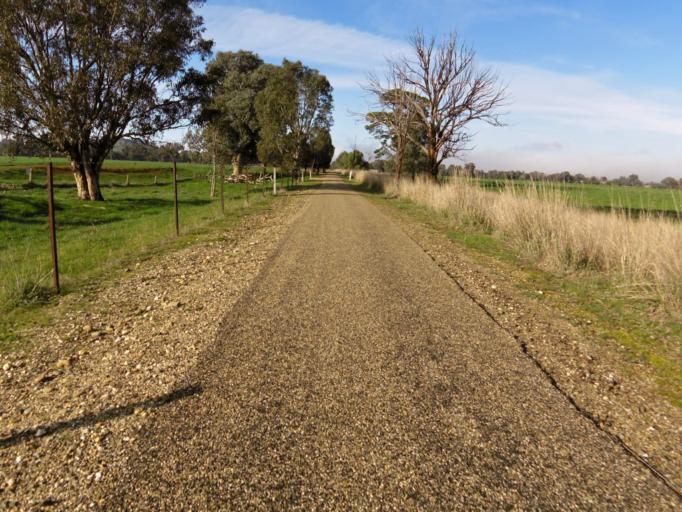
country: AU
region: Victoria
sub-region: Wangaratta
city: Wangaratta
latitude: -36.4233
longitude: 146.5503
